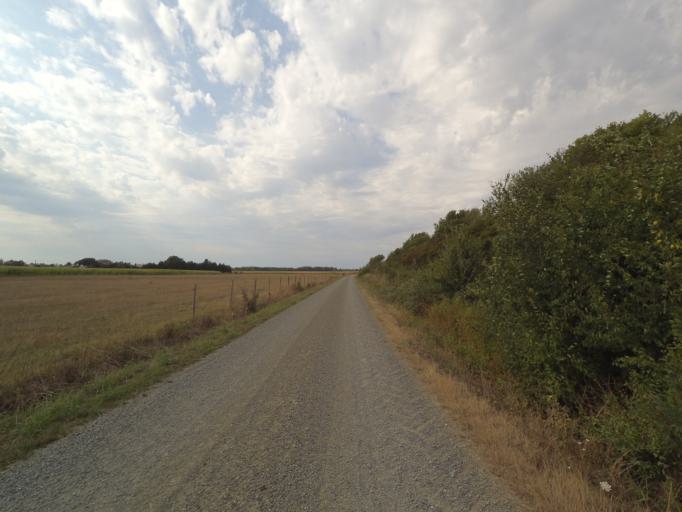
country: FR
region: Pays de la Loire
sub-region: Departement de la Vendee
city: Bouffere
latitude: 46.9823
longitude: -1.3772
